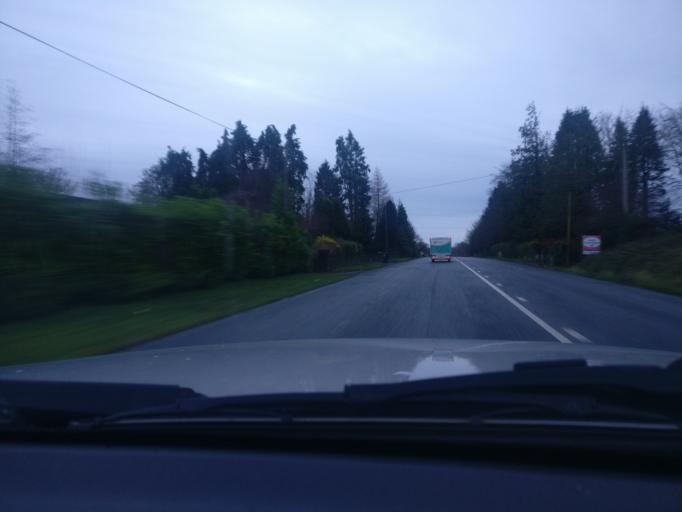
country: IE
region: Leinster
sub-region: An Mhi
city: Kells
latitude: 53.7039
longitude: -6.7953
